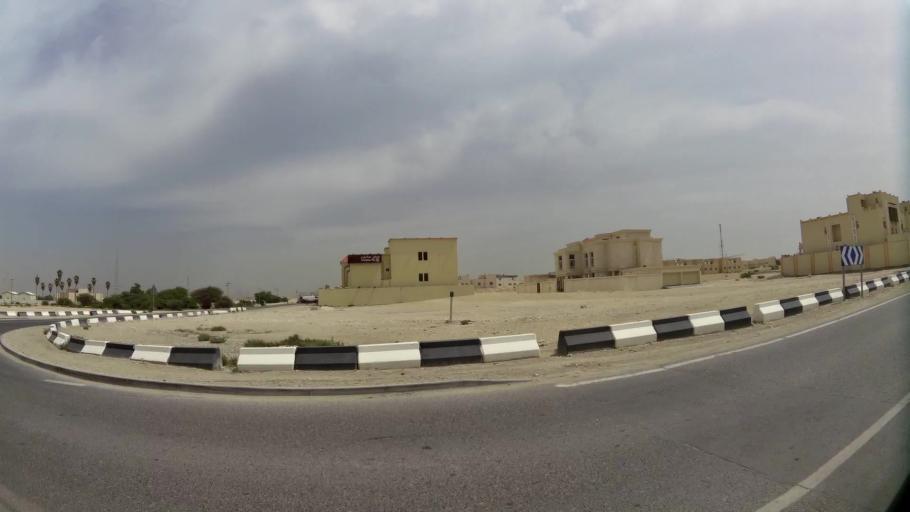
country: QA
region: Baladiyat ar Rayyan
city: Ar Rayyan
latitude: 25.2694
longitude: 51.4615
